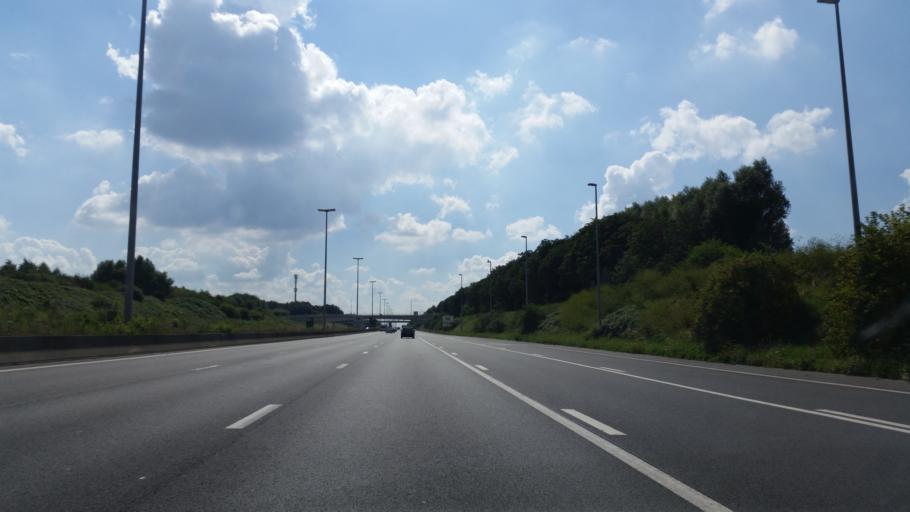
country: BE
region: Flanders
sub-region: Provincie West-Vlaanderen
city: Kortrijk
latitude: 50.8040
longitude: 3.2610
